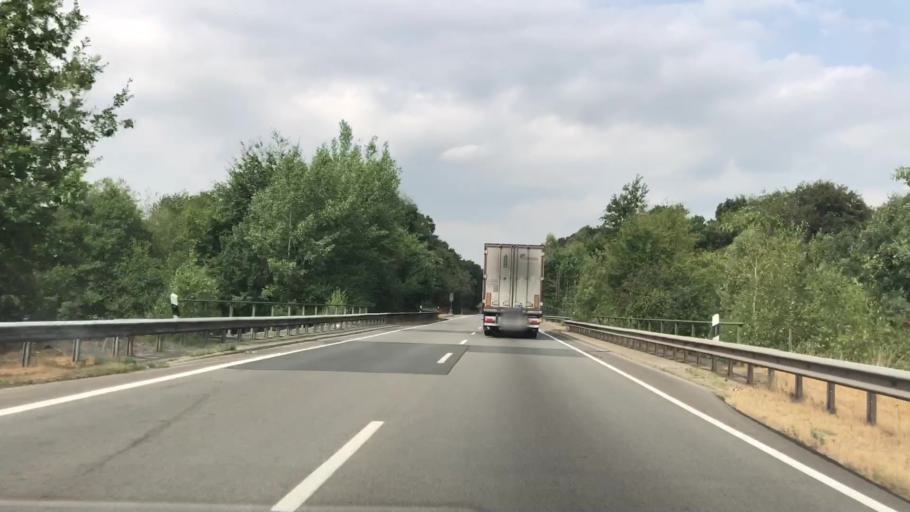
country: DE
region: Lower Saxony
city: Meppen
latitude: 52.7168
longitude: 7.2859
